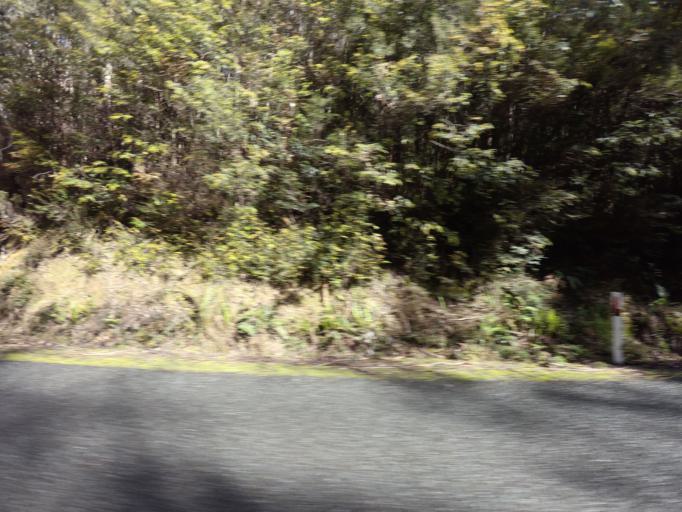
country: AU
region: Tasmania
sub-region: Derwent Valley
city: New Norfolk
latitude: -42.7471
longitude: 146.4139
